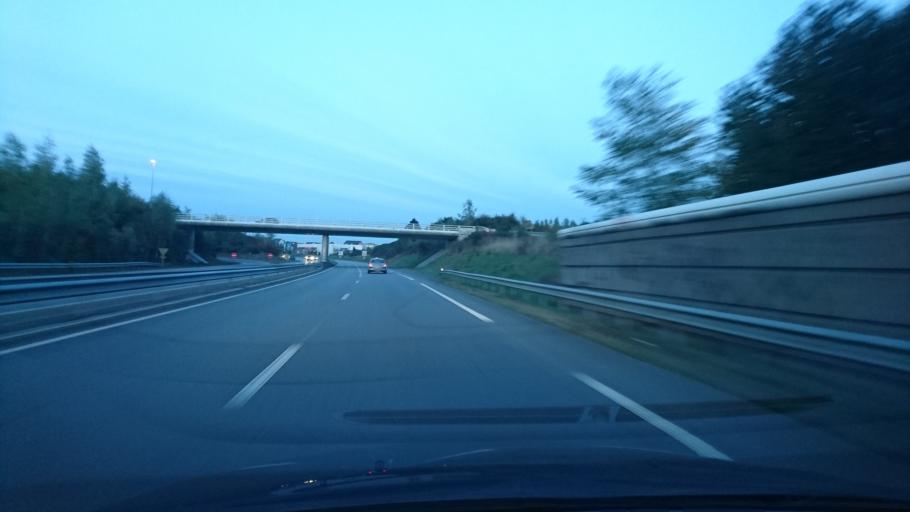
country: FR
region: Brittany
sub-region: Departement d'Ille-et-Vilaine
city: Bruz
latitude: 48.0264
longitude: -1.7691
